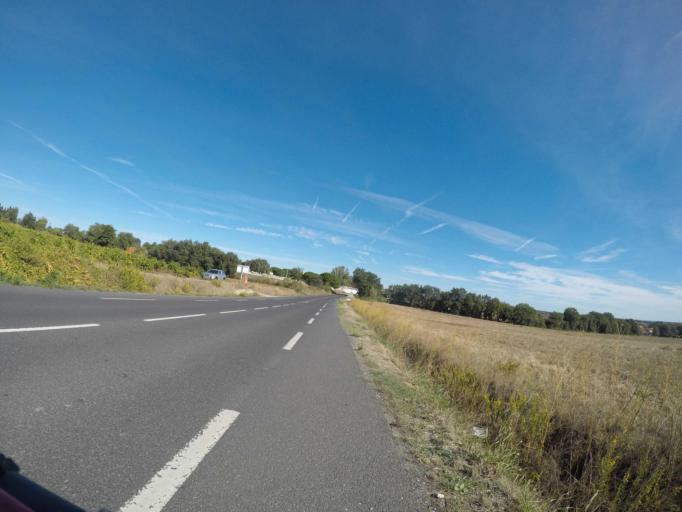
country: FR
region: Languedoc-Roussillon
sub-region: Departement des Pyrenees-Orientales
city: Ponteilla
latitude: 42.6215
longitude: 2.8115
